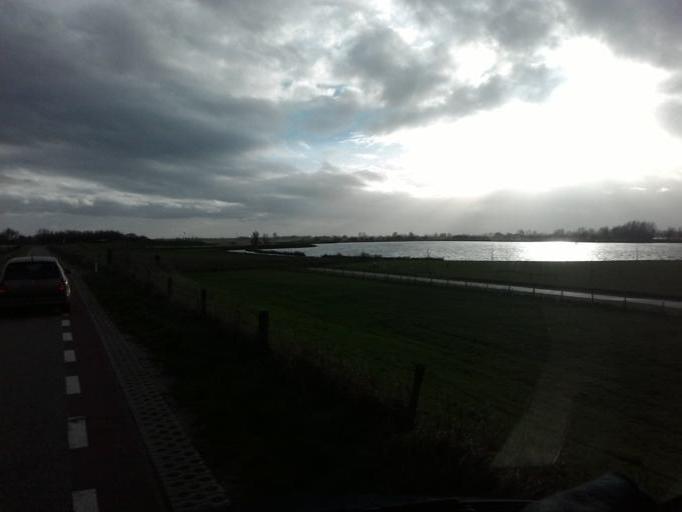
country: NL
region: Utrecht
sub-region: Gemeente Houten
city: Houten
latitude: 51.9877
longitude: 5.1510
